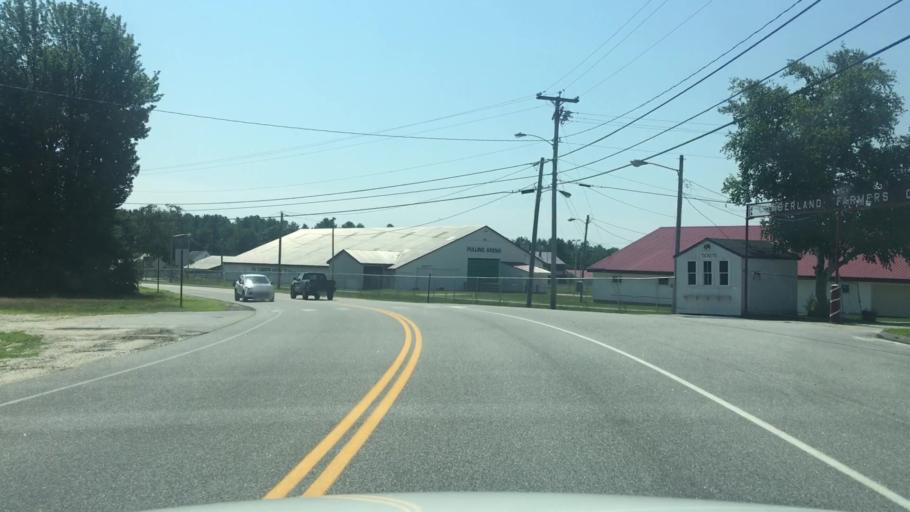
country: US
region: Maine
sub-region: Cumberland County
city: Cumberland Center
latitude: 43.8122
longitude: -70.2887
